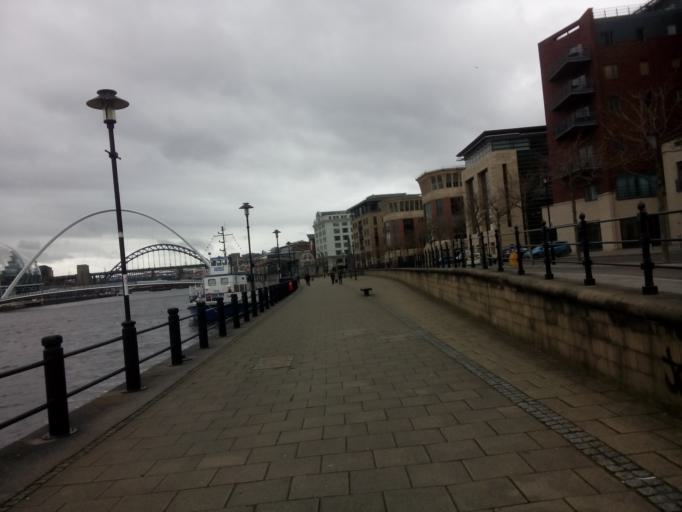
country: GB
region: England
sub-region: Gateshead
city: Gateshead
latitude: 54.9711
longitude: -1.5958
